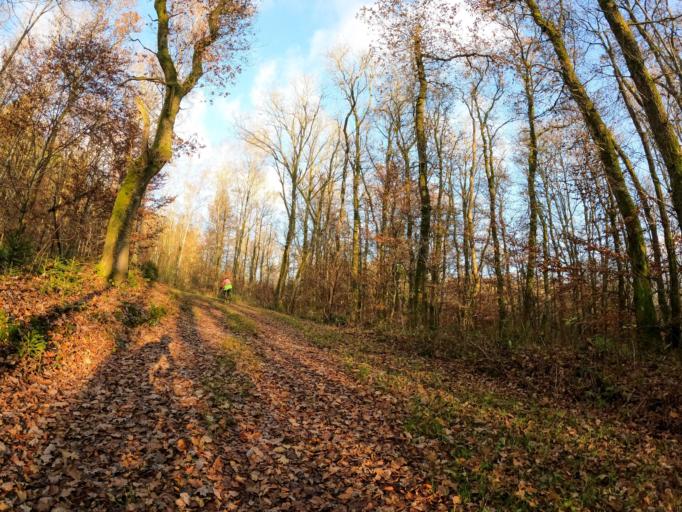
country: LU
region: Diekirch
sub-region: Canton de Wiltz
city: Bavigne
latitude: 49.9675
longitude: 5.8244
